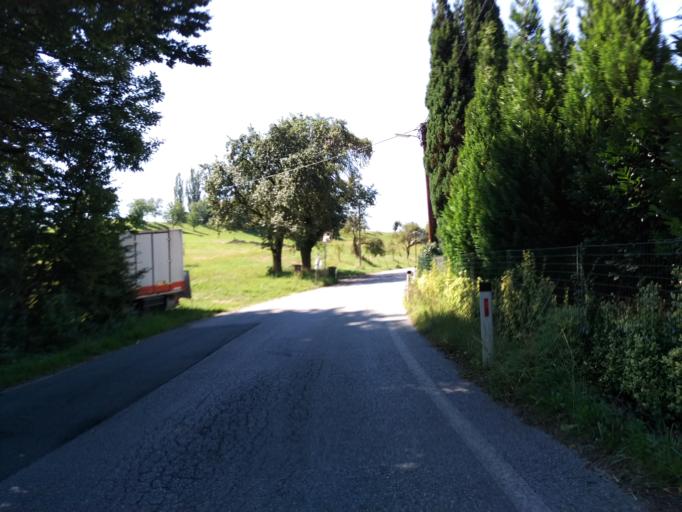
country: AT
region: Styria
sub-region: Politischer Bezirk Graz-Umgebung
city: Hart bei Graz
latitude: 47.0672
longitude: 15.5206
